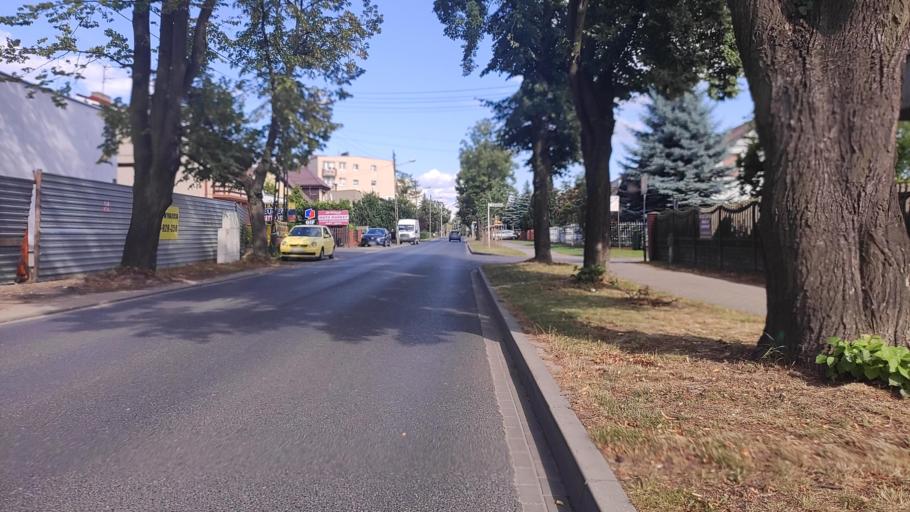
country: PL
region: Greater Poland Voivodeship
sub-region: Powiat poznanski
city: Swarzedz
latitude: 52.4130
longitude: 17.0810
